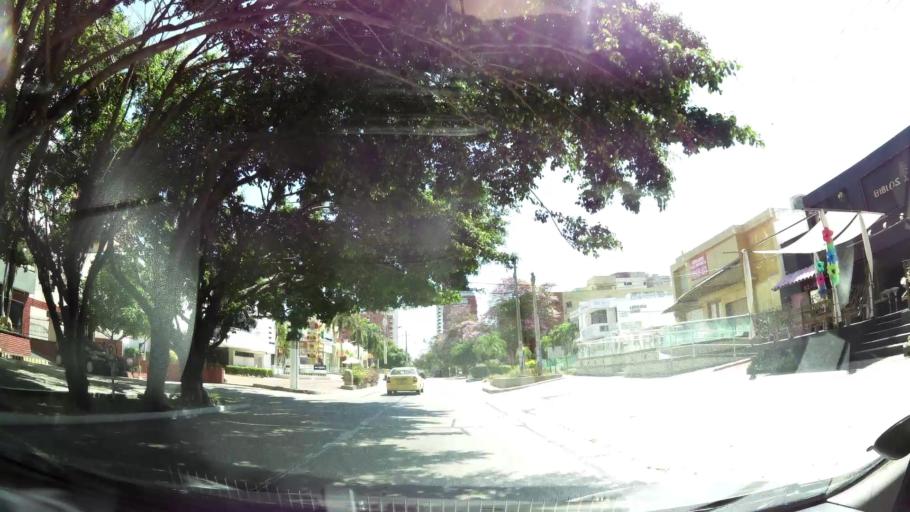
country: CO
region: Atlantico
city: Barranquilla
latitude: 11.0052
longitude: -74.8159
